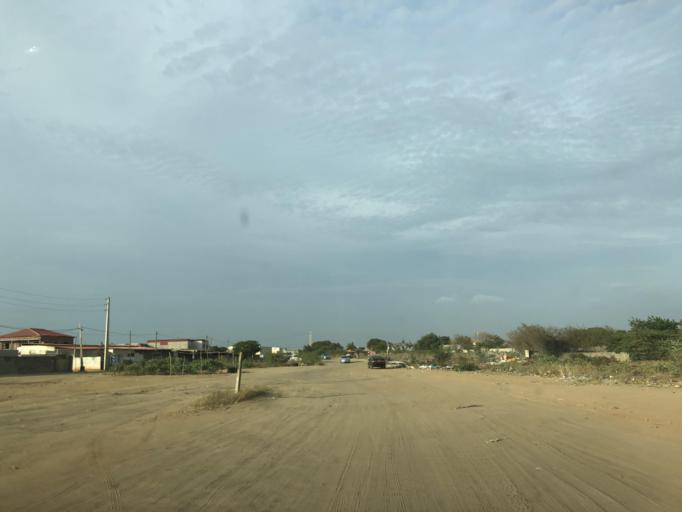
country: AO
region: Luanda
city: Luanda
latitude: -8.9113
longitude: 13.3148
